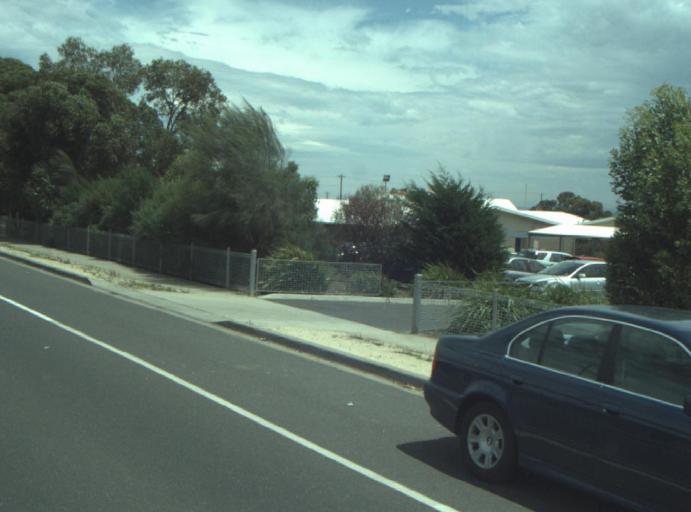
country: AU
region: Victoria
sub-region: Greater Geelong
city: Leopold
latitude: -38.1865
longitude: 144.4649
